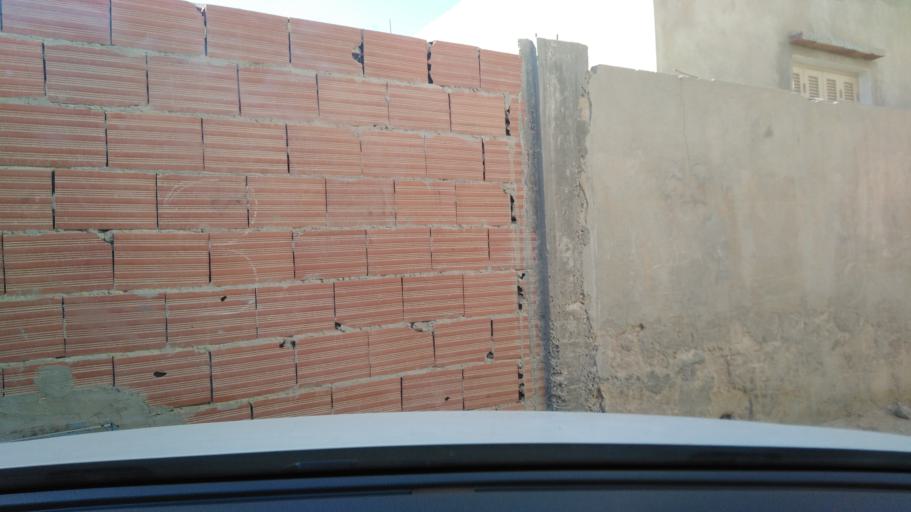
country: TN
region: Qabis
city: Gabes
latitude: 33.9398
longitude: 10.0693
